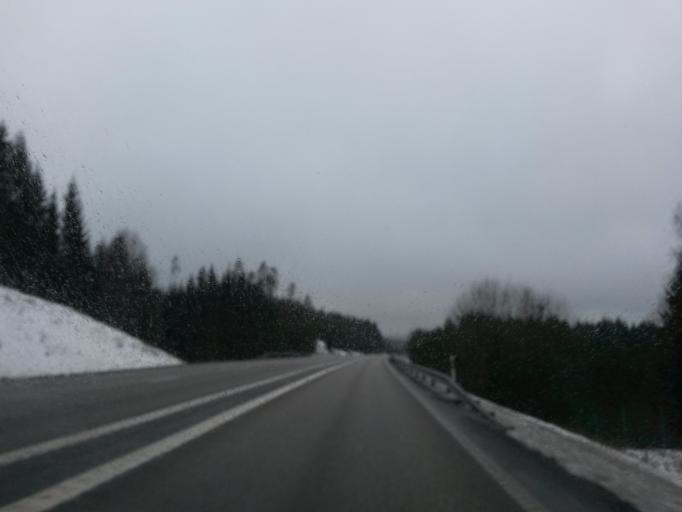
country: SE
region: Vaestra Goetaland
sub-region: Marks Kommun
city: Fritsla
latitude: 57.5162
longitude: 12.7604
